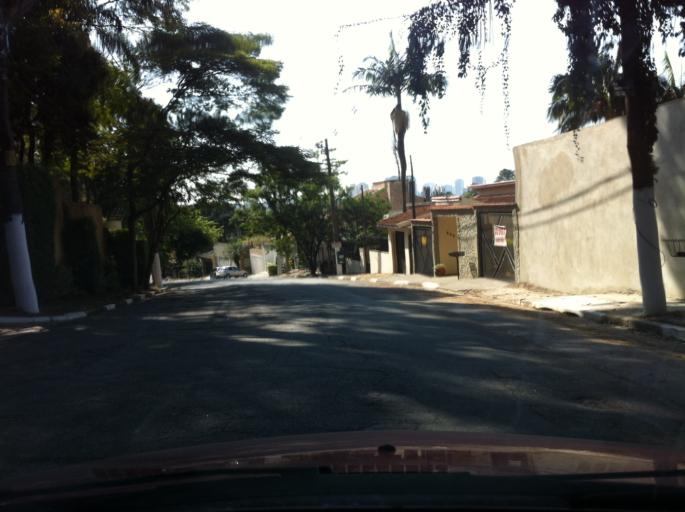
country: BR
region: Sao Paulo
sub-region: Diadema
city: Diadema
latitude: -23.6393
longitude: -46.6888
